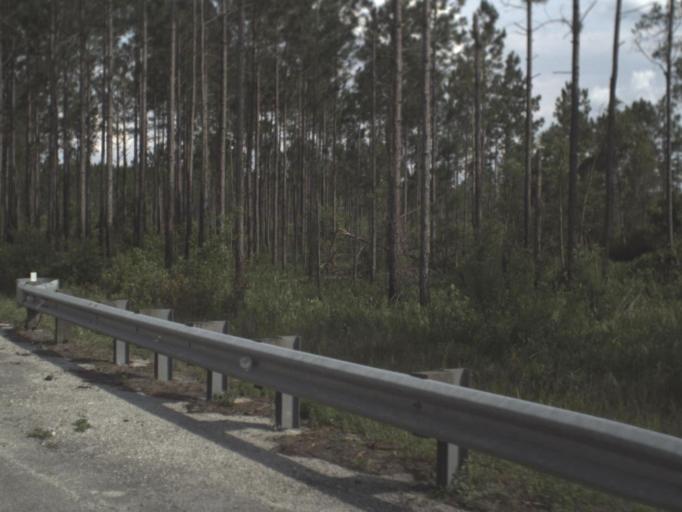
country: US
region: Florida
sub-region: Baker County
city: Macclenny
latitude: 30.5633
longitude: -82.3913
